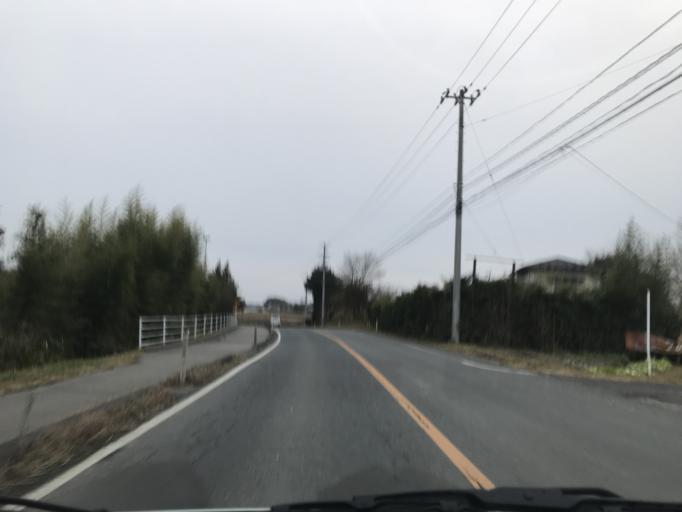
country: JP
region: Miyagi
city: Wakuya
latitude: 38.6760
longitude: 141.1124
